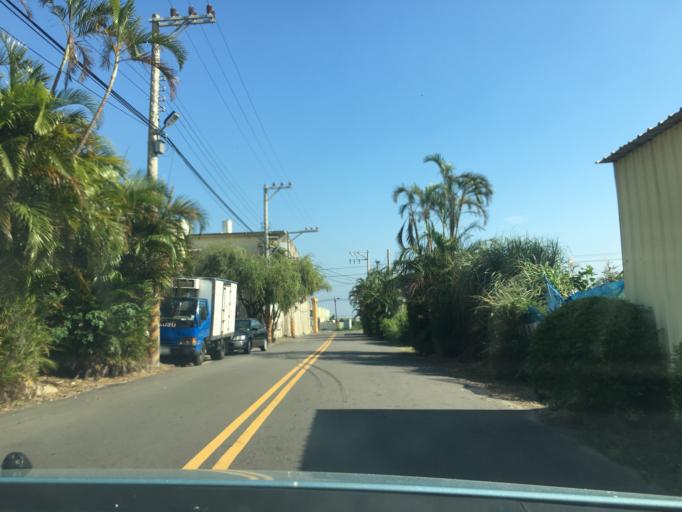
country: TW
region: Taiwan
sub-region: Hsinchu
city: Hsinchu
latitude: 24.8083
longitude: 120.9212
